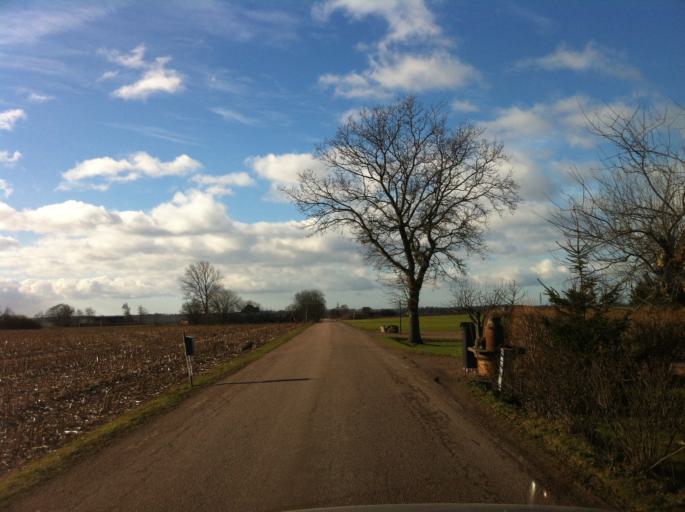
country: SE
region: Skane
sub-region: Landskrona
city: Asmundtorp
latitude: 55.9423
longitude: 12.9595
